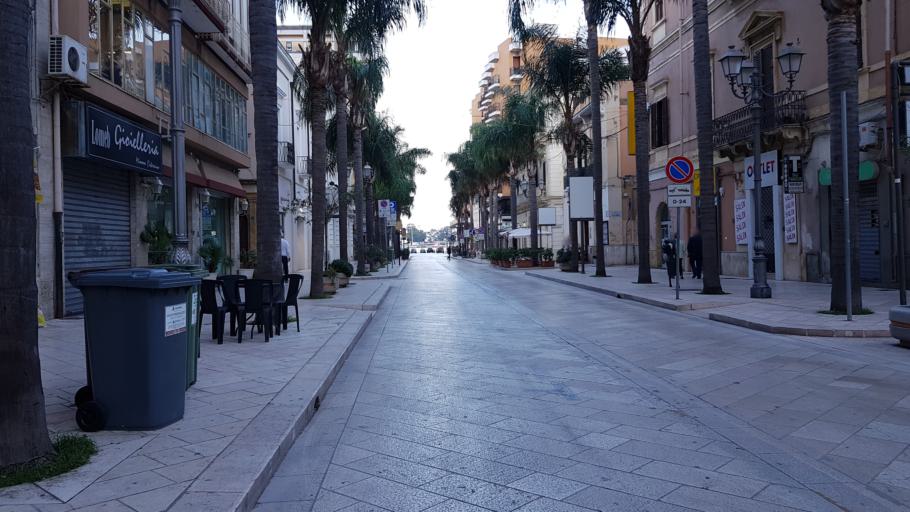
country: IT
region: Apulia
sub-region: Provincia di Brindisi
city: Brindisi
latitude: 40.6386
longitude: 17.9472
